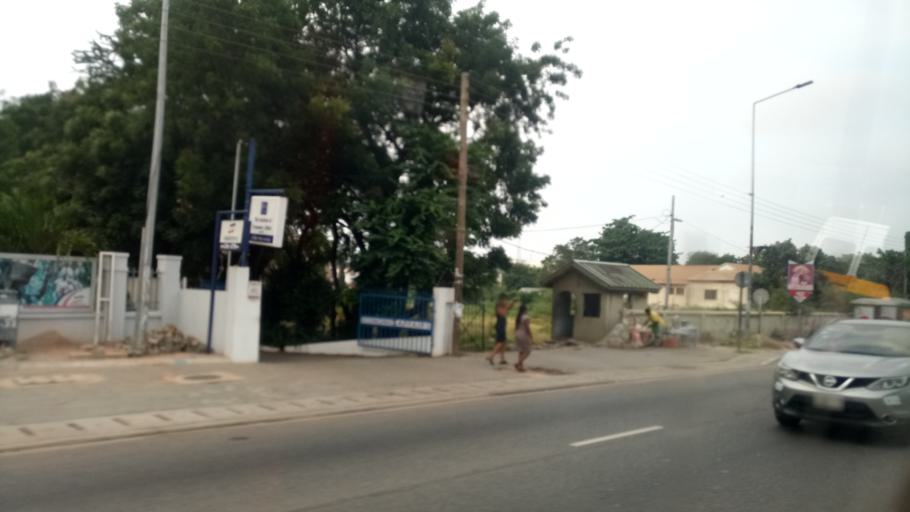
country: GH
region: Greater Accra
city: Accra
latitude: 5.5655
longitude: -0.1939
